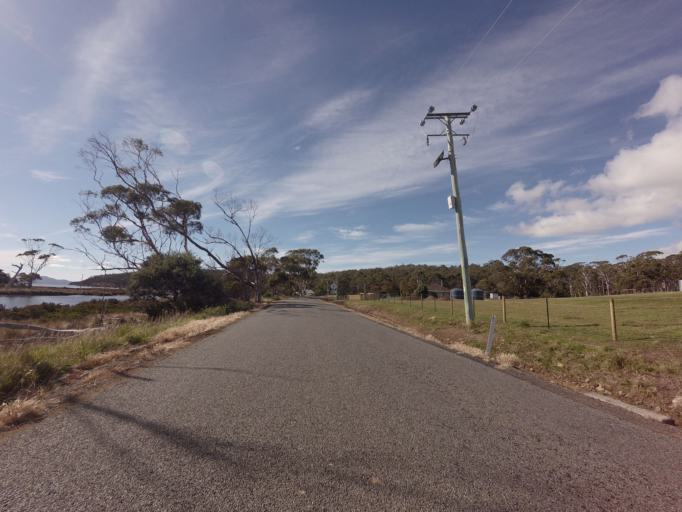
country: AU
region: Tasmania
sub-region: Clarence
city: Sandford
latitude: -43.0271
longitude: 147.7238
